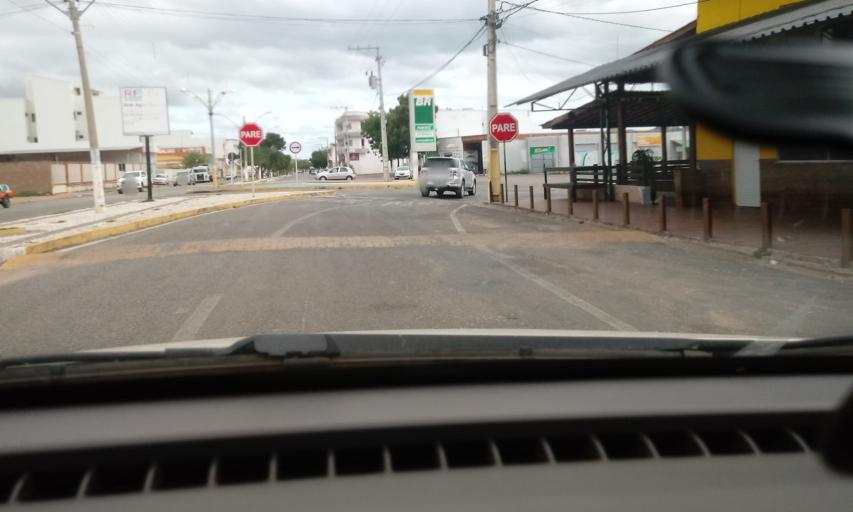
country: BR
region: Bahia
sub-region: Guanambi
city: Guanambi
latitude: -14.2136
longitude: -42.7878
